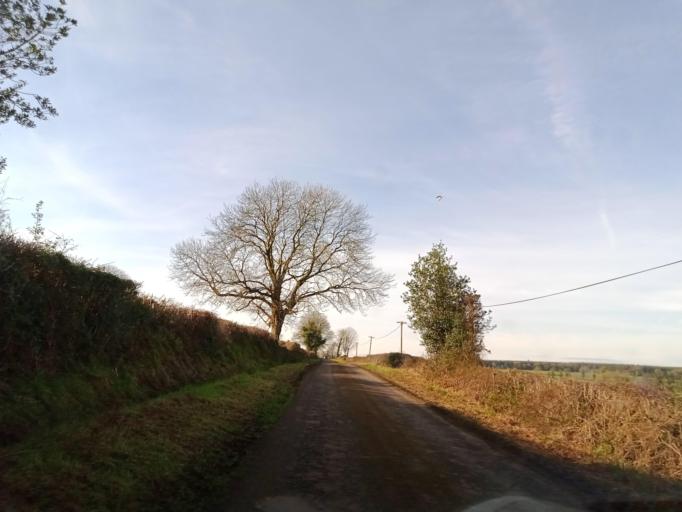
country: IE
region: Munster
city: Fethard
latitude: 52.5633
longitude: -7.5774
